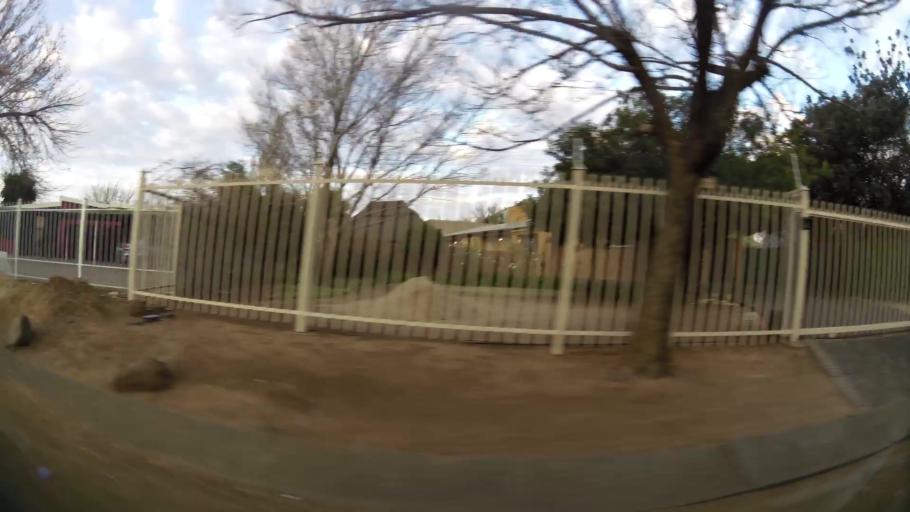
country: ZA
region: Orange Free State
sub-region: Mangaung Metropolitan Municipality
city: Bloemfontein
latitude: -29.1426
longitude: 26.1742
